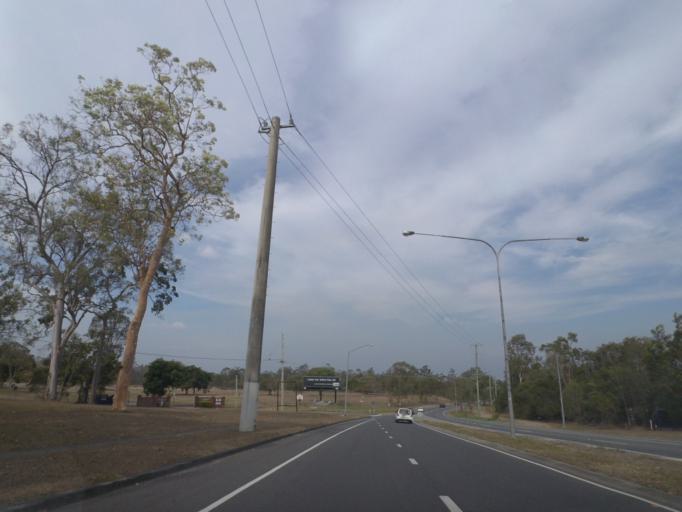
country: AU
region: Queensland
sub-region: Brisbane
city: Inala
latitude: -27.5932
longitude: 152.9927
